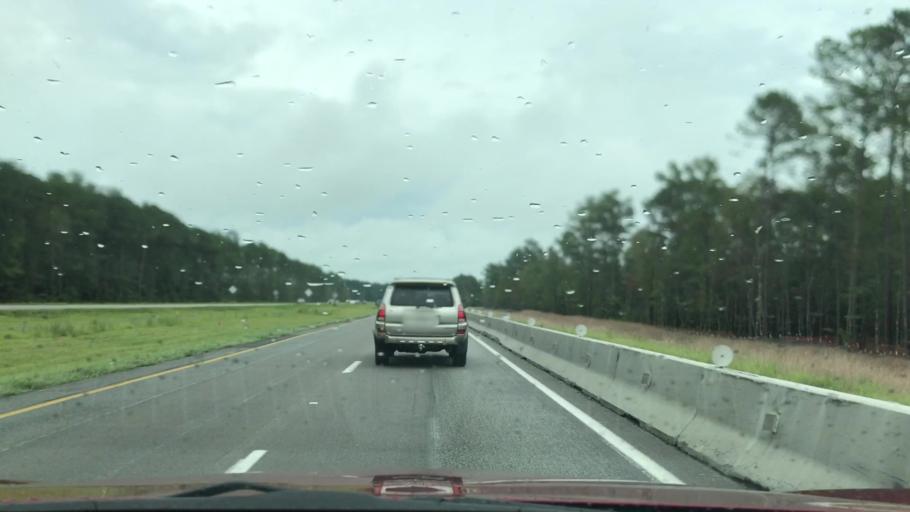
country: US
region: South Carolina
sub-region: Dorchester County
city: Ridgeville
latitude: 33.1253
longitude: -80.2861
